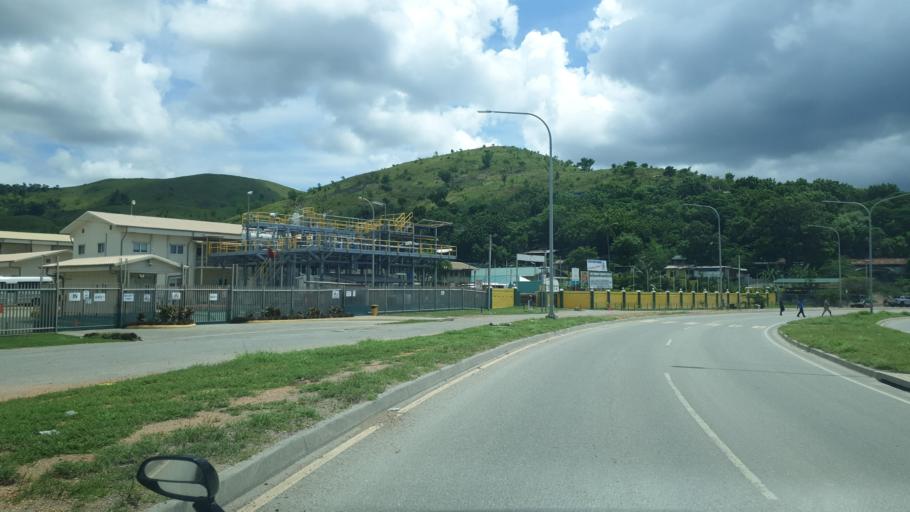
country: PG
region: National Capital
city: Port Moresby
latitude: -9.4455
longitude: 147.1441
